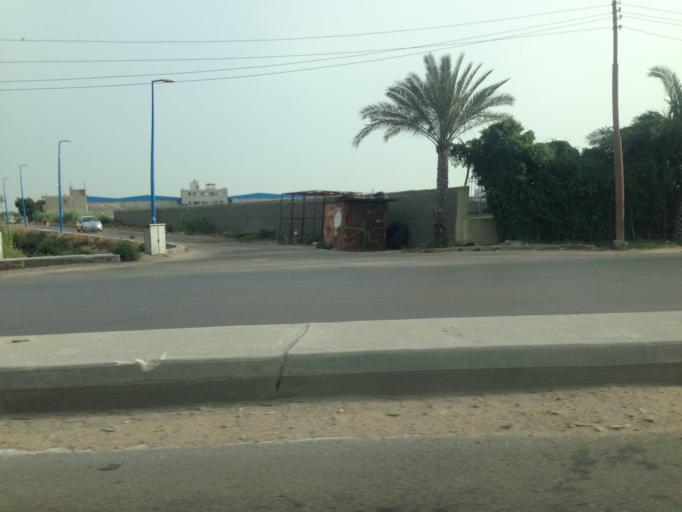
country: EG
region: Alexandria
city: Alexandria
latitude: 31.2016
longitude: 30.0200
